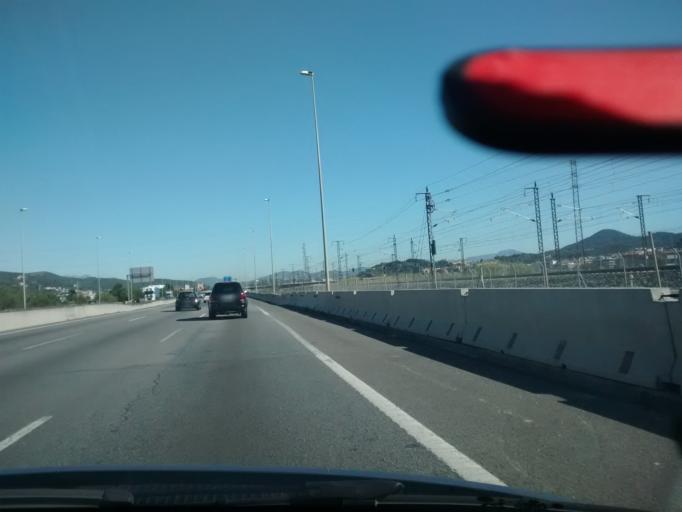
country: ES
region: Catalonia
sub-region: Provincia de Barcelona
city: Sant Vicenc dels Horts
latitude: 41.4009
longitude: 2.0141
